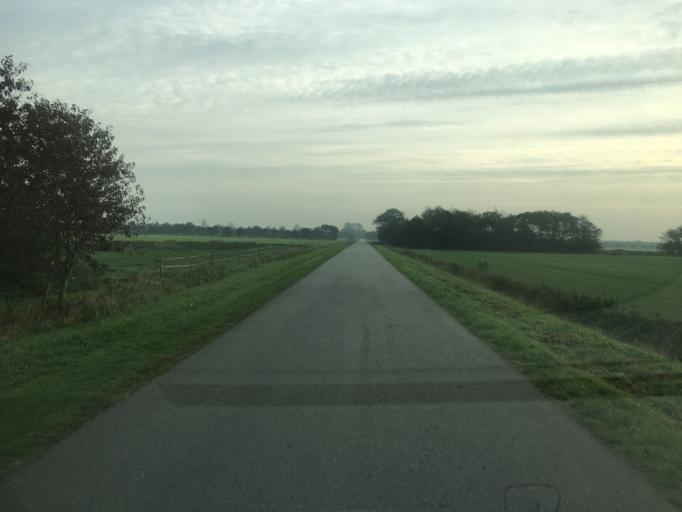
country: DK
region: South Denmark
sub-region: Tonder Kommune
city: Logumkloster
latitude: 55.1020
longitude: 9.0308
